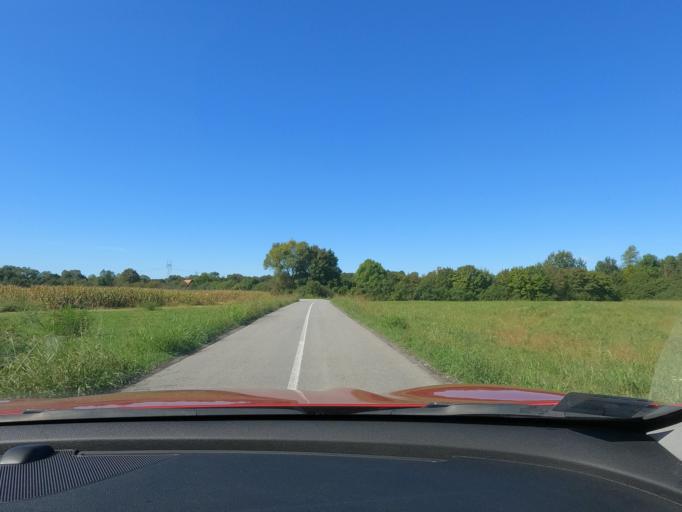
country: HR
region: Sisacko-Moslavacka
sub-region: Grad Sisak
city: Sisak
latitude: 45.4828
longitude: 16.3301
